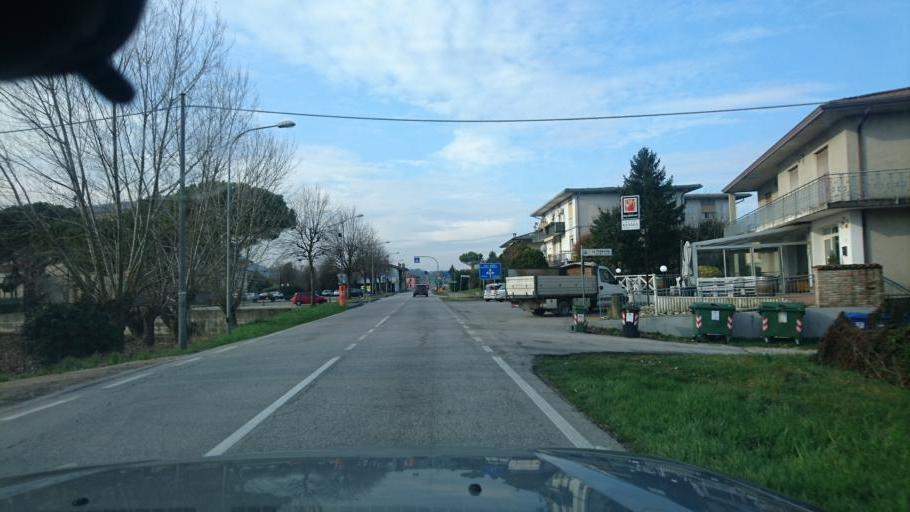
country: IT
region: Veneto
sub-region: Provincia di Padova
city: Cervarese Santa Croce
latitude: 45.4036
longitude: 11.6955
